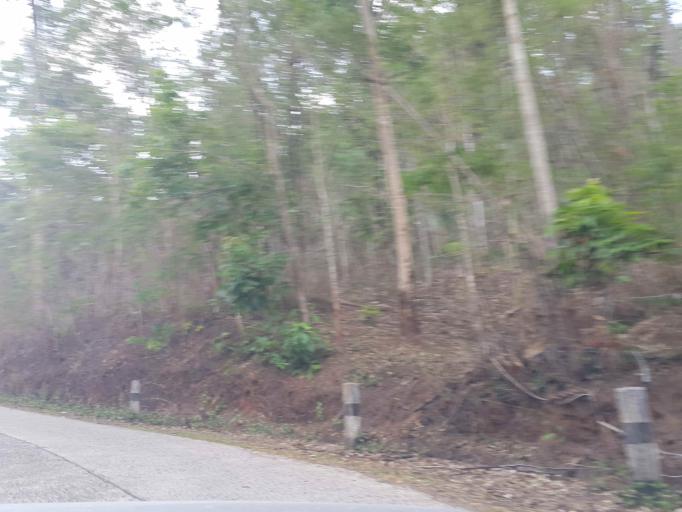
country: TH
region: Chiang Mai
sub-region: Amphoe Chiang Dao
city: Chiang Dao
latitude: 19.3842
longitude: 98.7759
